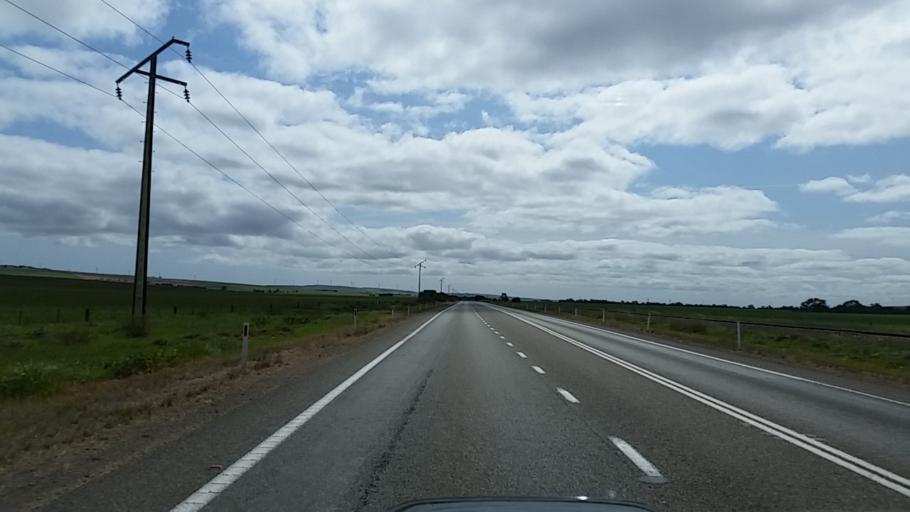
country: AU
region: South Australia
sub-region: Port Pirie City and Dists
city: Crystal Brook
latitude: -33.5320
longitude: 138.2093
